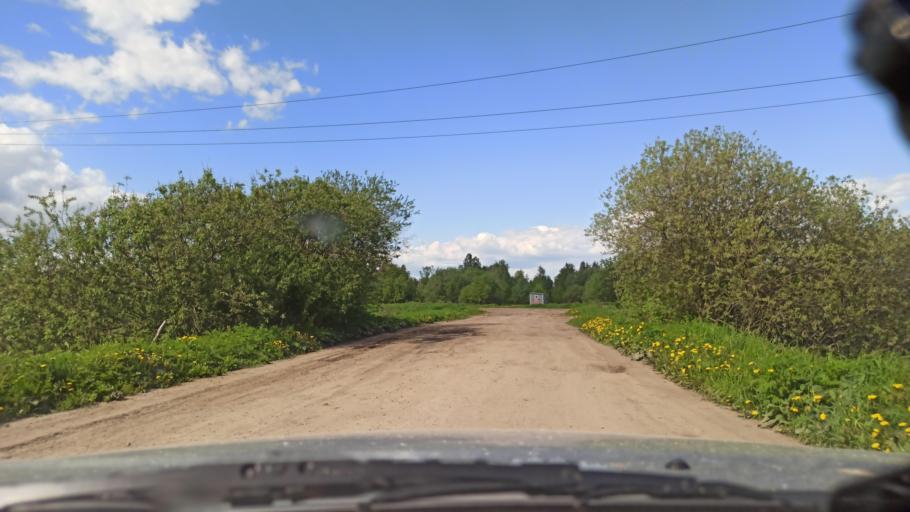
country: RU
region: Vologda
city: Vologda
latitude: 59.3403
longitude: 39.8382
